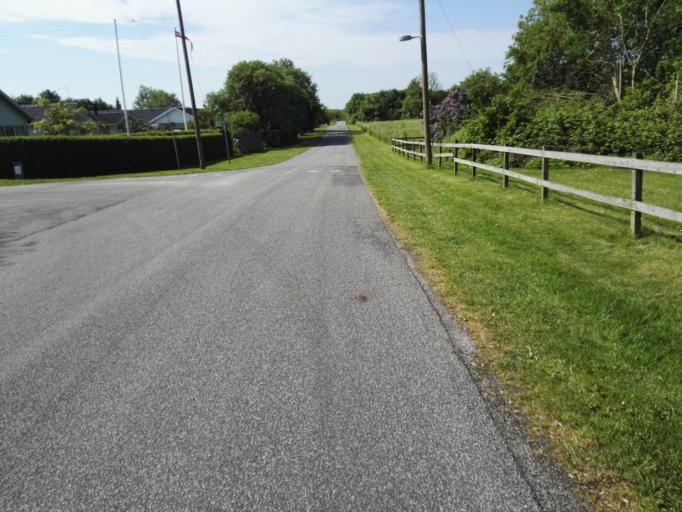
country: DK
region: Capital Region
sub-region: Frederikssund Kommune
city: Skibby
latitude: 55.7476
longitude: 11.9513
